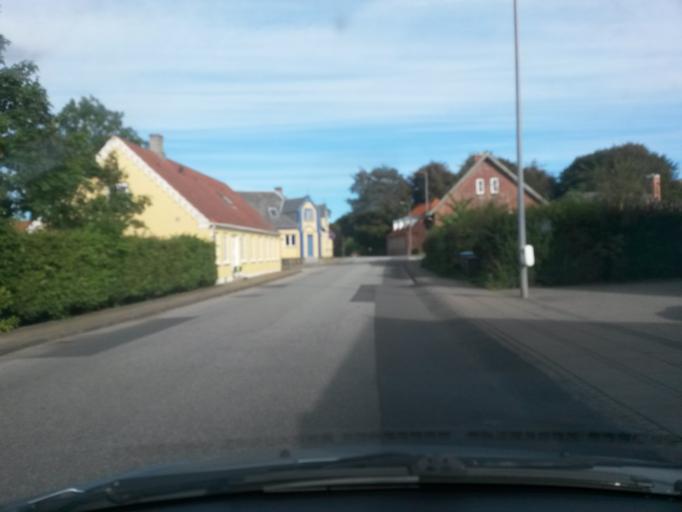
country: DK
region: Central Jutland
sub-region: Silkeborg Kommune
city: Kjellerup
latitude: 56.2877
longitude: 9.4221
